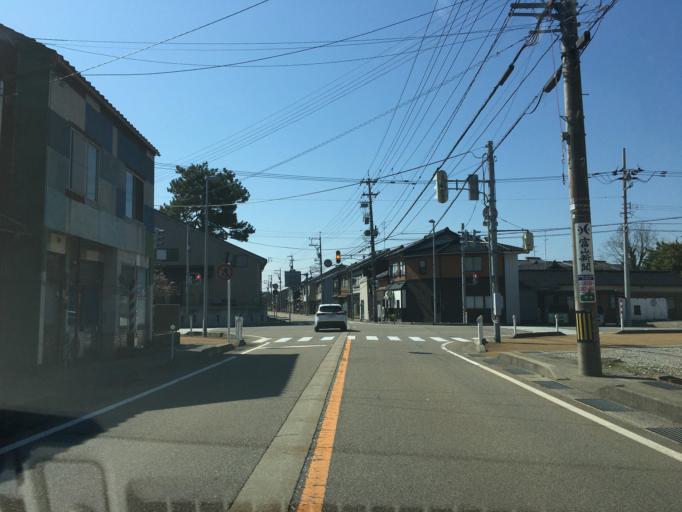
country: JP
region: Toyama
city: Himi
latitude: 36.8722
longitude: 136.9831
